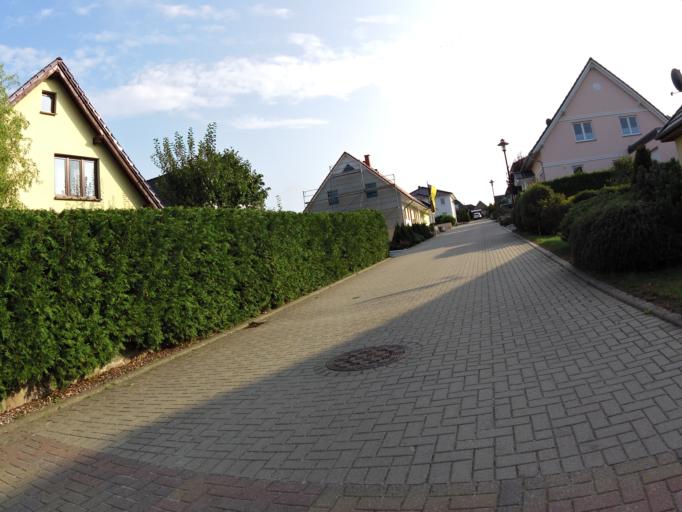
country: DE
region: Mecklenburg-Vorpommern
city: Seebad Bansin
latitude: 53.9580
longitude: 14.1475
